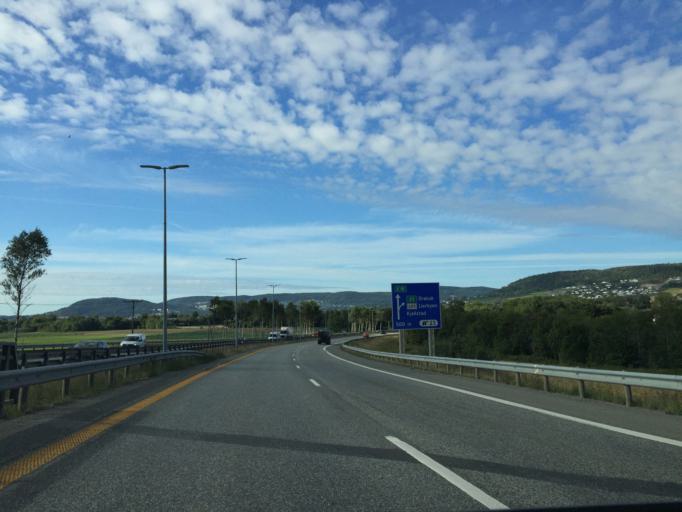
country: NO
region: Buskerud
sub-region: Lier
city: Lierbyen
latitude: 59.7760
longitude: 10.2759
